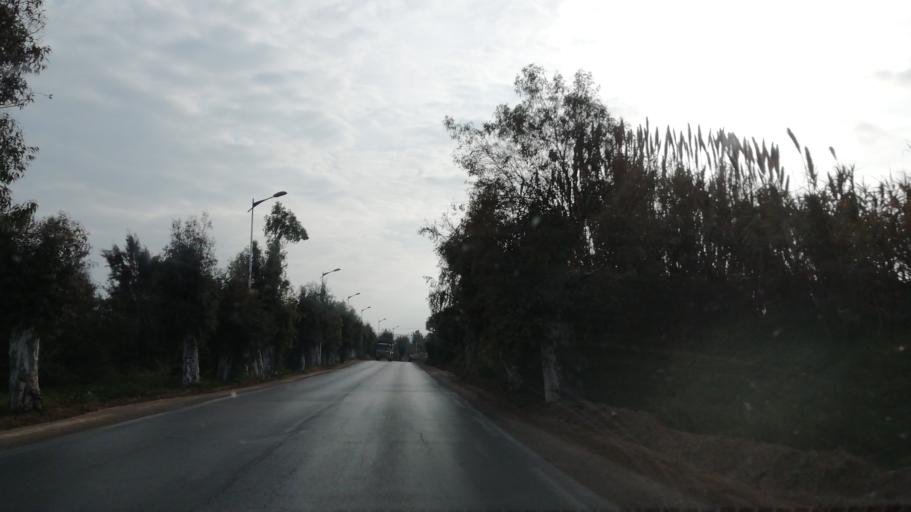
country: DZ
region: Mostaganem
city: Mostaganem
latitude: 35.8754
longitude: 0.0783
